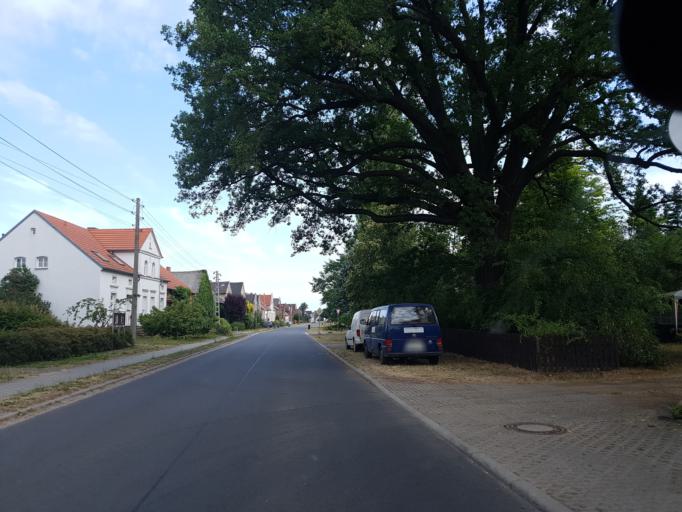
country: DE
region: Brandenburg
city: Luckau
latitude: 51.8367
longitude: 13.6408
